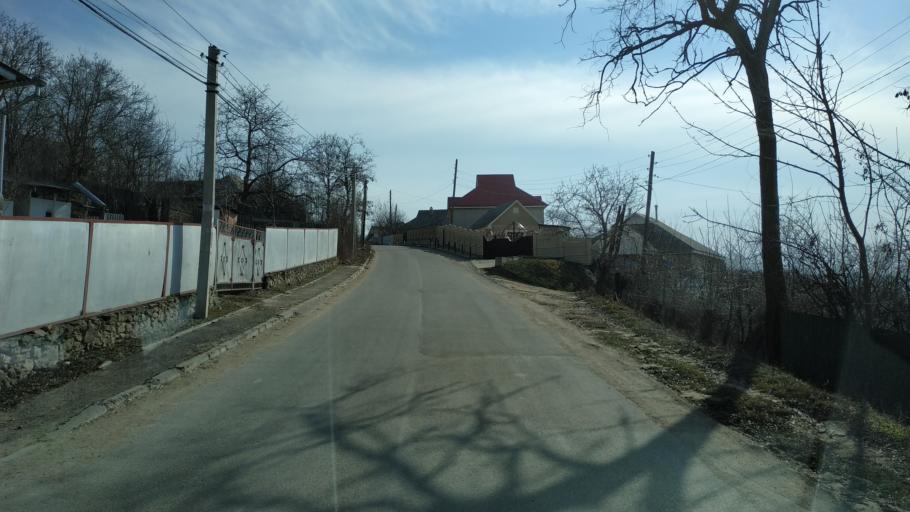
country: MD
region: Nisporeni
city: Nisporeni
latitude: 47.1729
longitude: 28.1295
